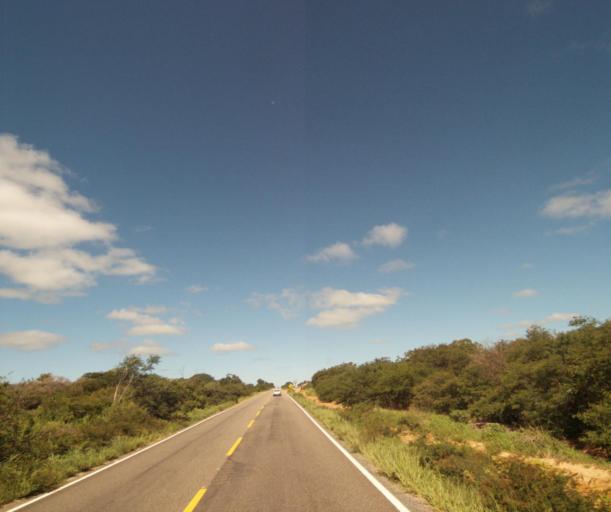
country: BR
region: Bahia
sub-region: Palmas De Monte Alto
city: Palmas de Monte Alto
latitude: -14.2400
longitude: -43.0441
